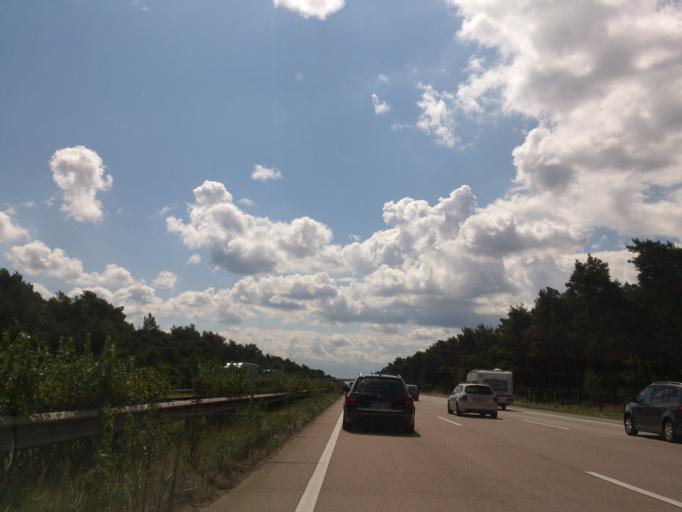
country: DE
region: Lower Saxony
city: Lindwedel
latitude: 52.6346
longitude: 9.7185
